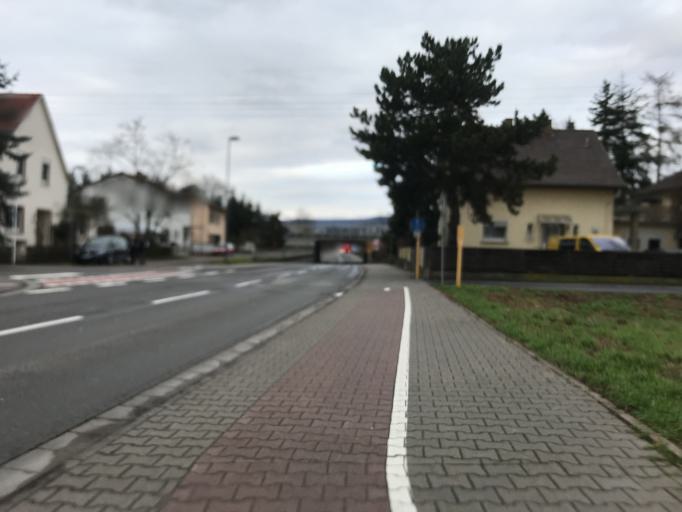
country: DE
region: Rheinland-Pfalz
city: Ingelheim am Rhein
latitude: 49.9796
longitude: 8.0335
